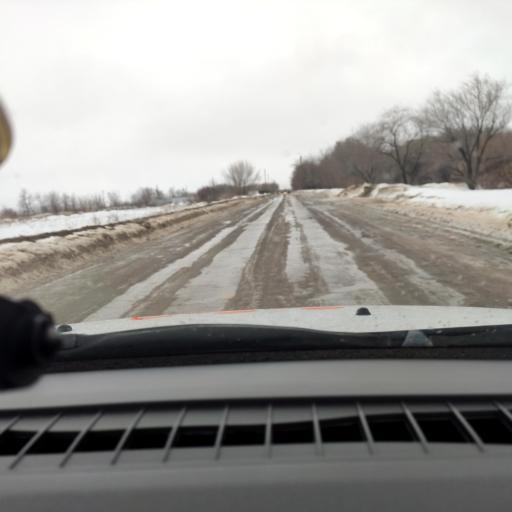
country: RU
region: Samara
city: Chapayevsk
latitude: 52.9939
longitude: 49.7713
